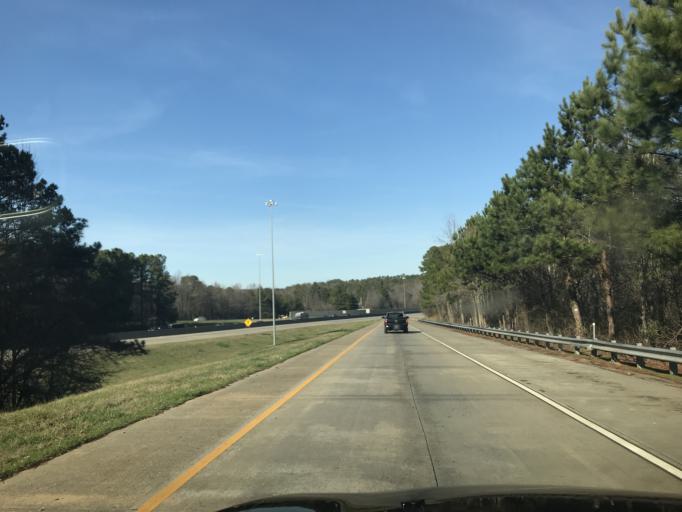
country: US
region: Georgia
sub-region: Fulton County
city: Palmetto
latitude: 33.5009
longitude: -84.6373
